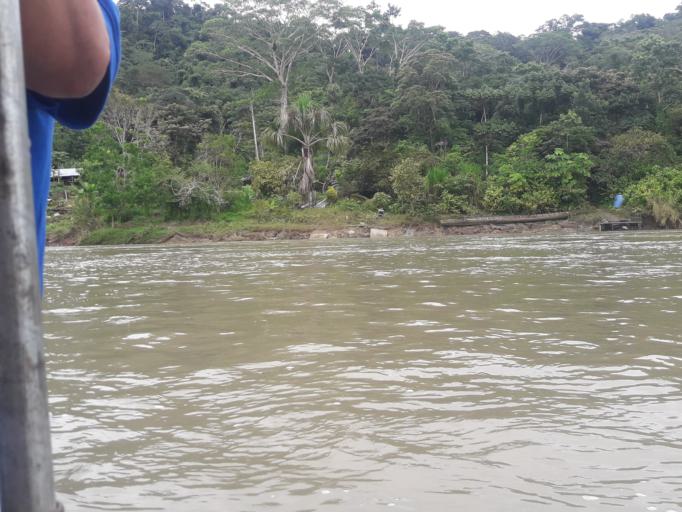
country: EC
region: Orellana
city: Boca Suno
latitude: -0.8764
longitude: -77.2648
